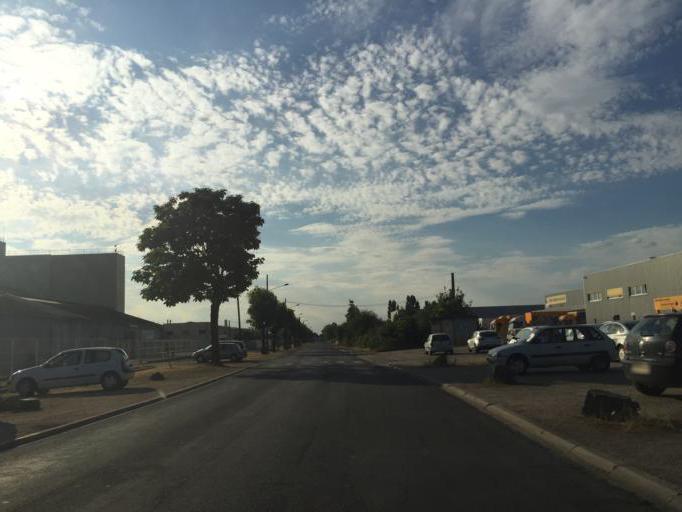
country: FR
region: Auvergne
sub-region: Departement de l'Allier
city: Yzeure
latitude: 46.5448
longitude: 3.3553
